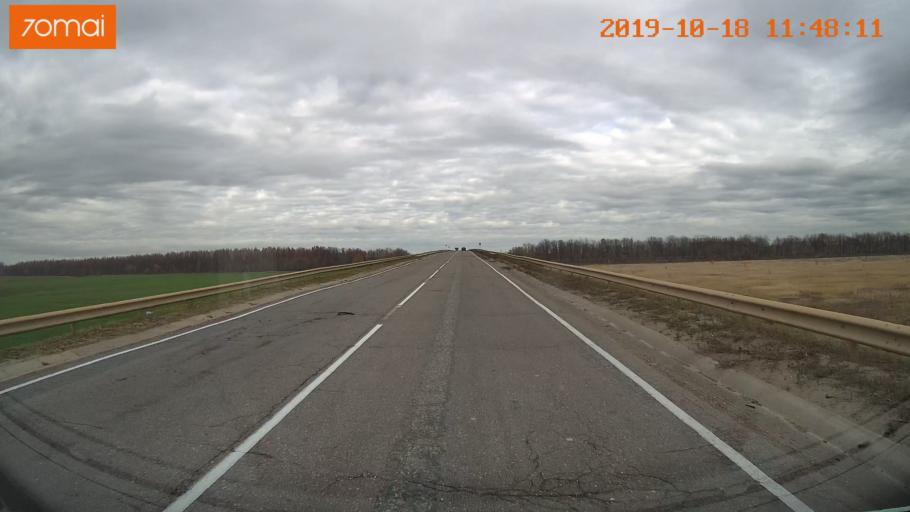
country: RU
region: Rjazan
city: Mikhaylov
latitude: 54.2367
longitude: 38.9814
